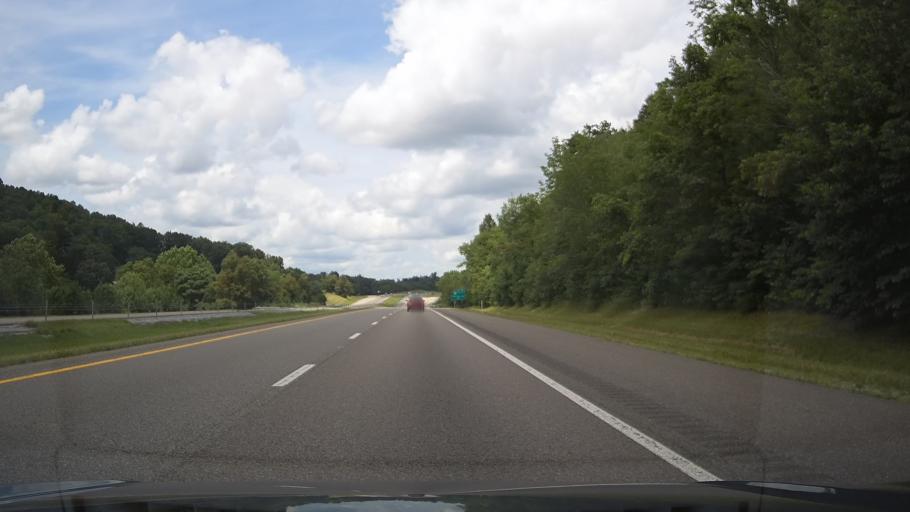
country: US
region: Tennessee
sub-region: Carter County
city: Pine Crest
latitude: 36.2616
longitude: -82.3221
